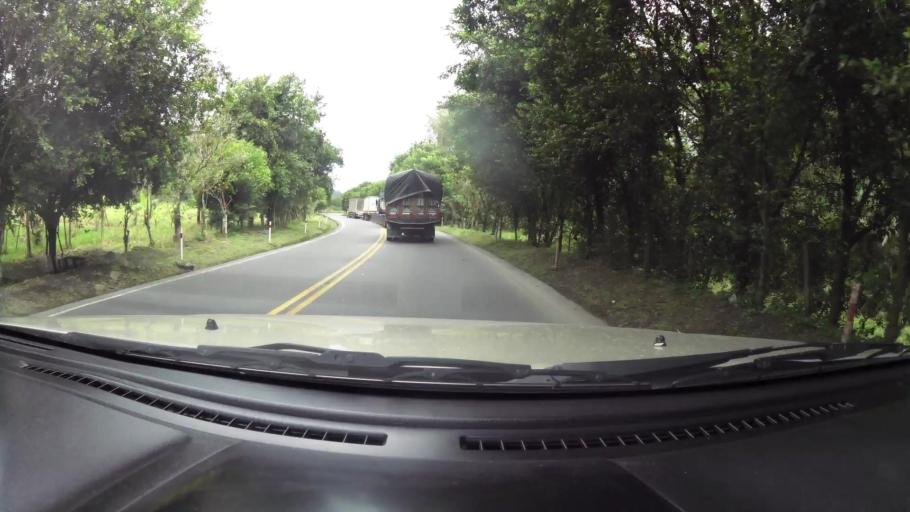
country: EC
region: Santo Domingo de los Tsachilas
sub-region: Canton Santo Domingo de los Colorados
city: Santo Domingo de los Colorados
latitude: -0.2873
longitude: -79.0677
